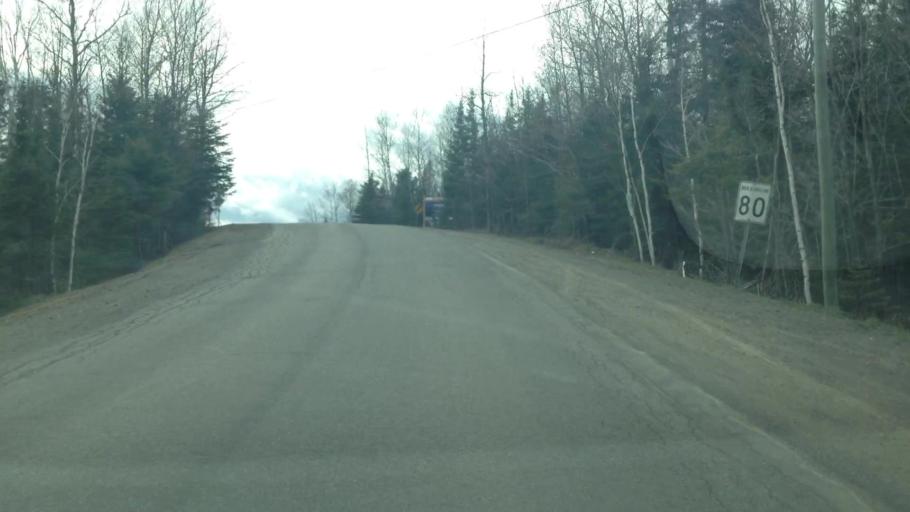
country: CA
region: Quebec
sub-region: Laurentides
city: Sainte-Adele
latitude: 46.0296
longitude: -74.0415
